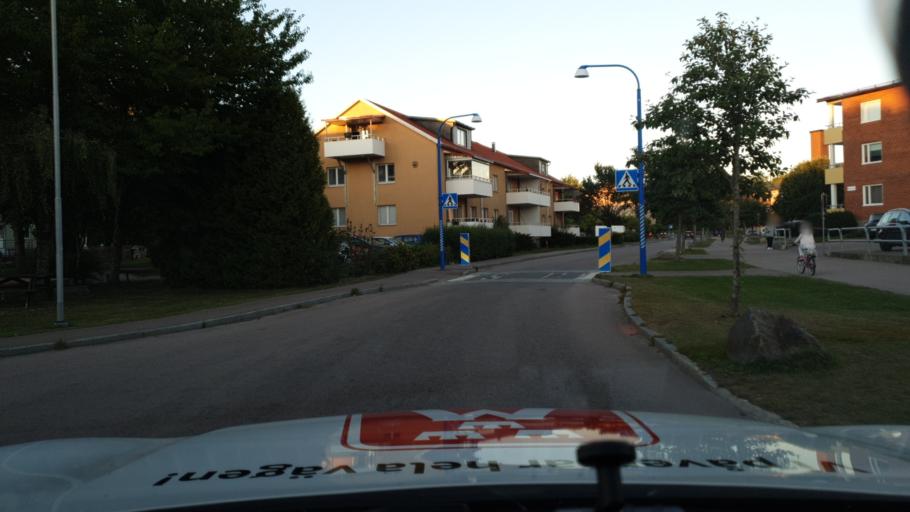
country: SE
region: Vaestmanland
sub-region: Hallstahammars Kommun
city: Hallstahammar
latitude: 59.6138
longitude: 16.2376
